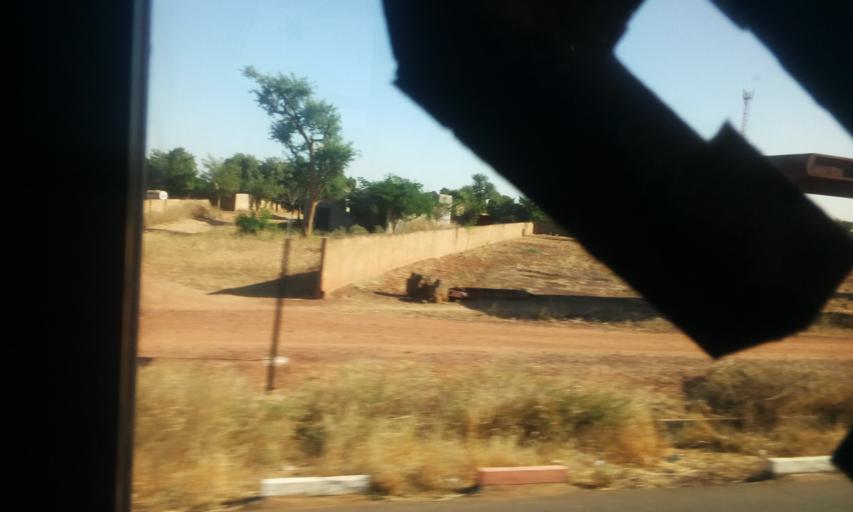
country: ML
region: Segou
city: Segou
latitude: 13.4134
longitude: -6.3242
